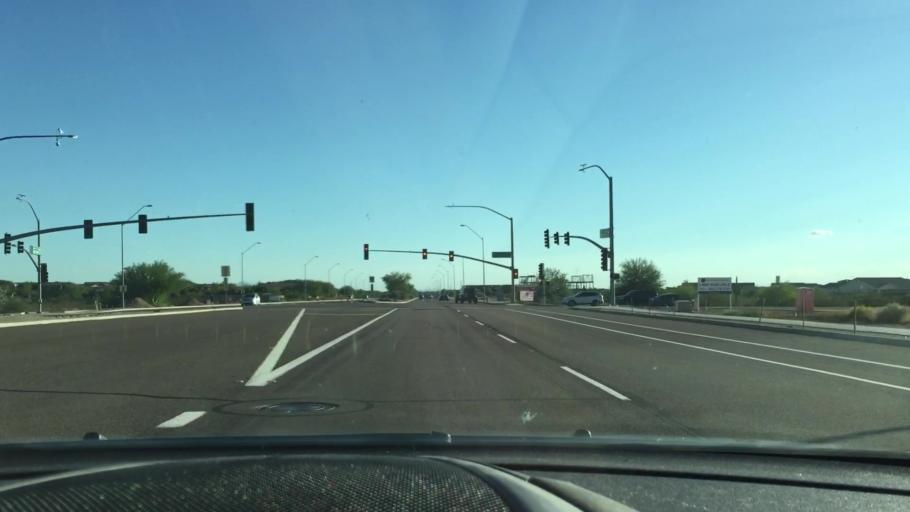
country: US
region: Arizona
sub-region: Maricopa County
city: Sun City West
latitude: 33.7257
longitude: -112.2672
